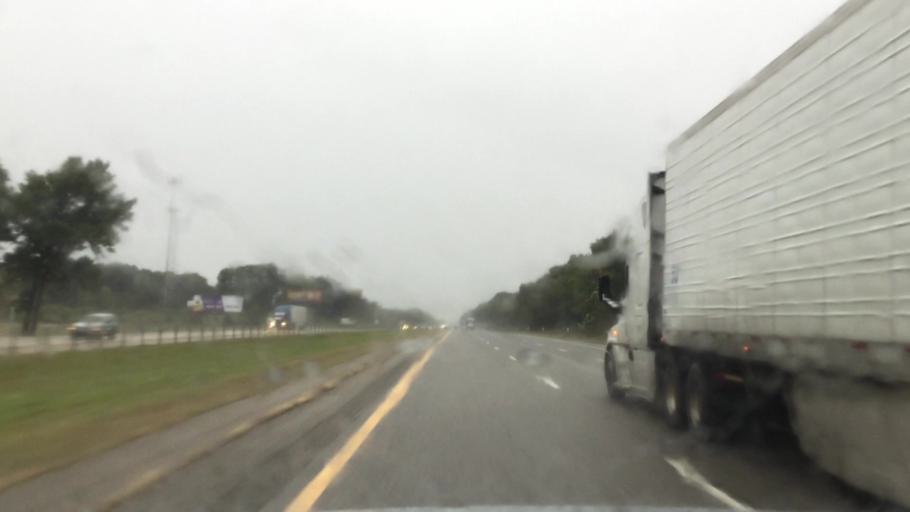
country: US
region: Michigan
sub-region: Van Buren County
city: Mattawan
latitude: 42.2228
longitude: -85.7892
